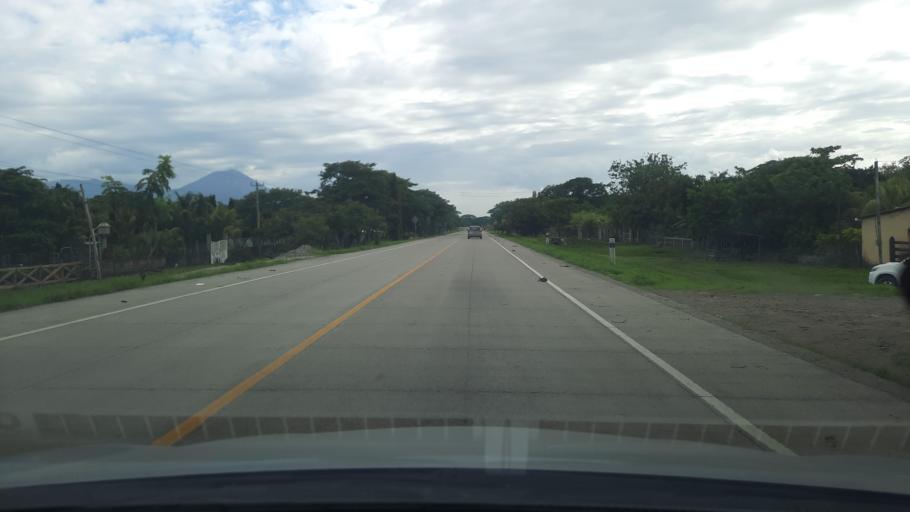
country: NI
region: Chinandega
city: Somotillo
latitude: 12.8399
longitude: -86.8844
